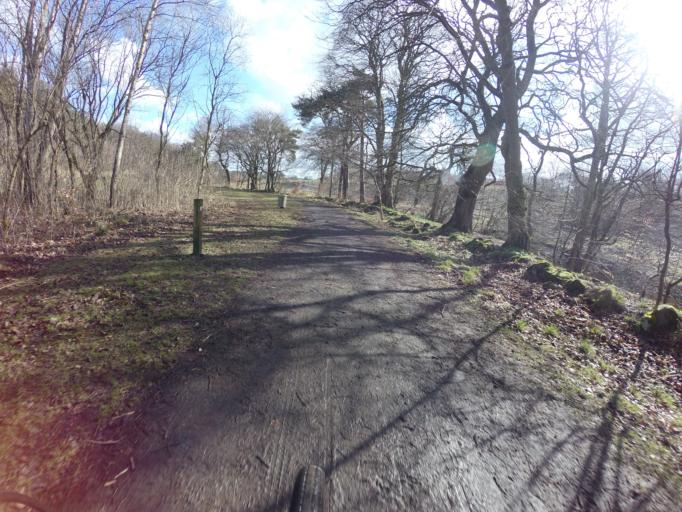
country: GB
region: Scotland
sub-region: West Lothian
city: Mid Calder
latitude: 55.8902
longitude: -3.4955
